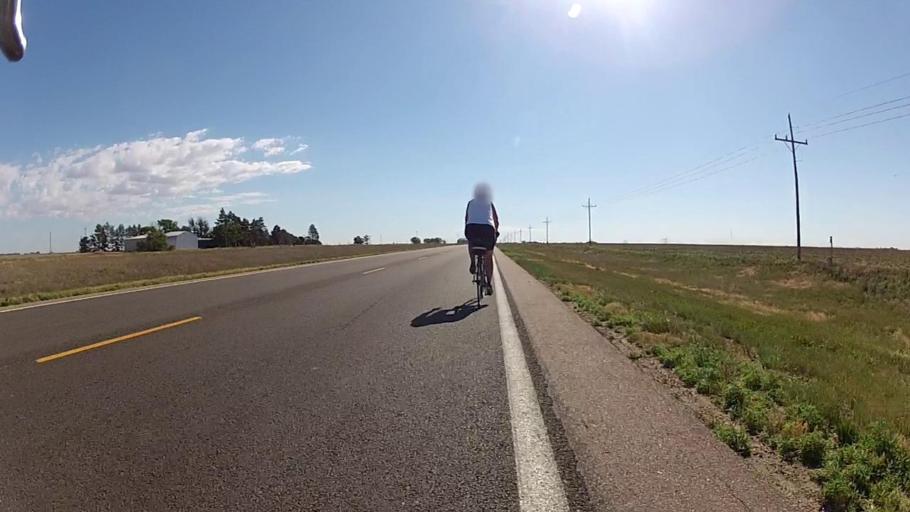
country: US
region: Kansas
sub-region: Gray County
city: Cimarron
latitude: 37.5894
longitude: -100.4780
